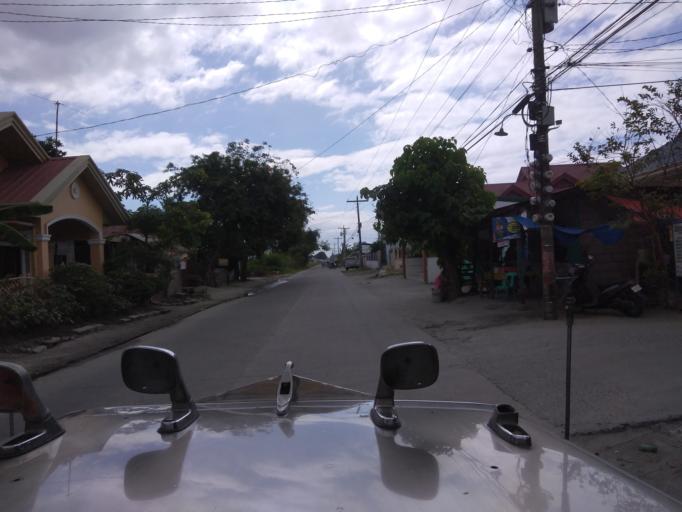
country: PH
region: Central Luzon
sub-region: Province of Pampanga
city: Anao
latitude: 15.1154
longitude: 120.7032
